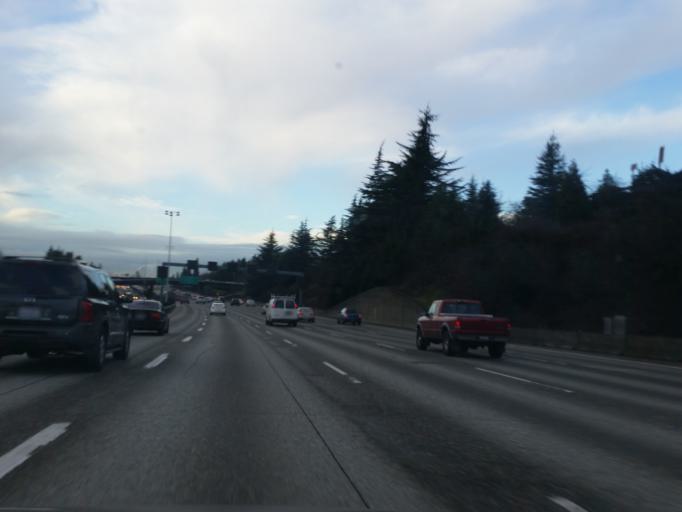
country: US
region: Washington
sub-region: King County
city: White Center
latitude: 47.5461
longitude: -122.3082
